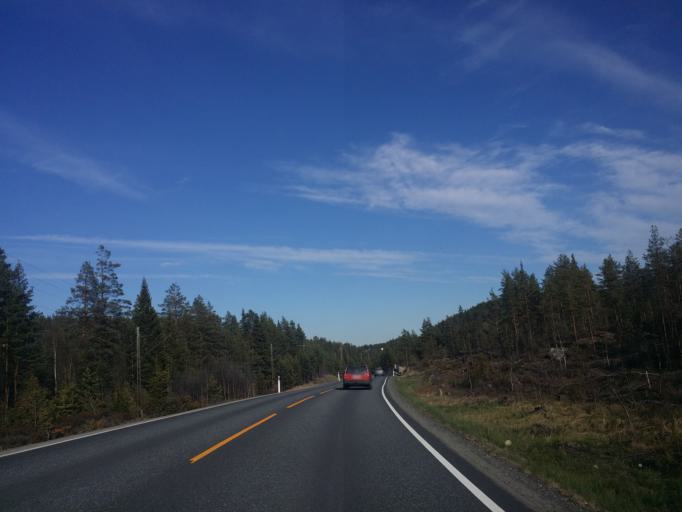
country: NO
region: Buskerud
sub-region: Kongsberg
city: Kongsberg
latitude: 59.6327
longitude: 9.5204
